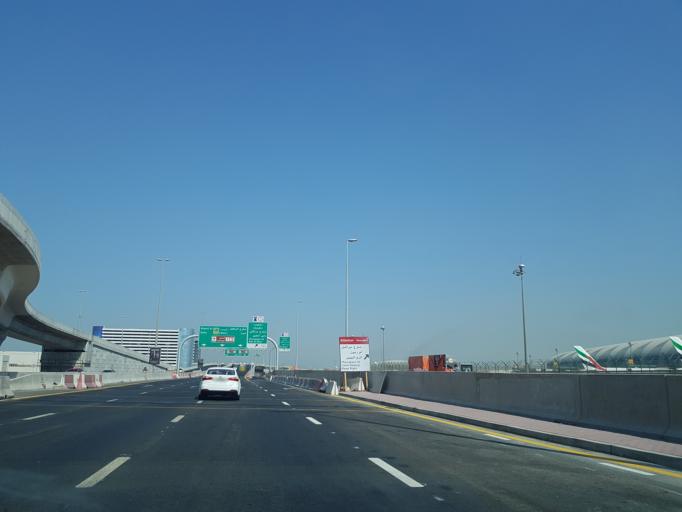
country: AE
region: Ash Shariqah
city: Sharjah
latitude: 25.2396
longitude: 55.3727
